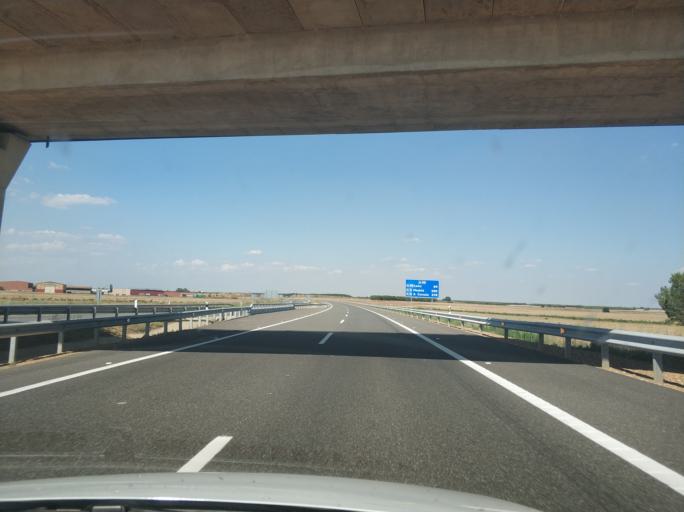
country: ES
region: Castille and Leon
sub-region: Provincia de Zamora
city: Santovenia
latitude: 41.8715
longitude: -5.7047
